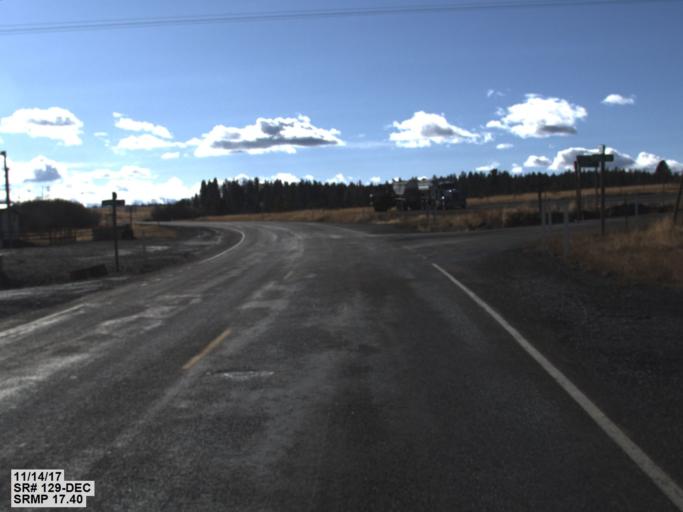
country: US
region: Washington
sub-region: Asotin County
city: Asotin
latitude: 46.1338
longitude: -117.1330
